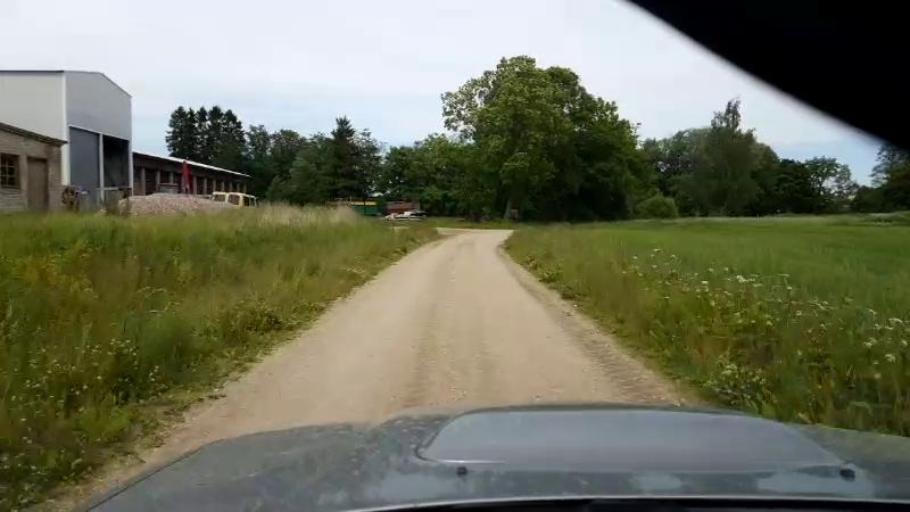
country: EE
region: Paernumaa
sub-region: Tootsi vald
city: Tootsi
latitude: 58.5372
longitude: 24.7337
